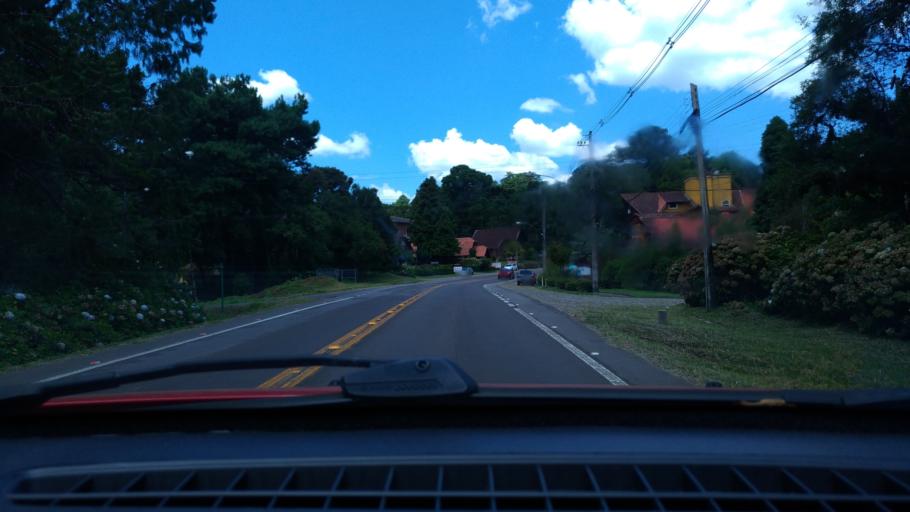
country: BR
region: Rio Grande do Sul
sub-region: Canela
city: Canela
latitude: -29.3538
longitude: -50.8318
